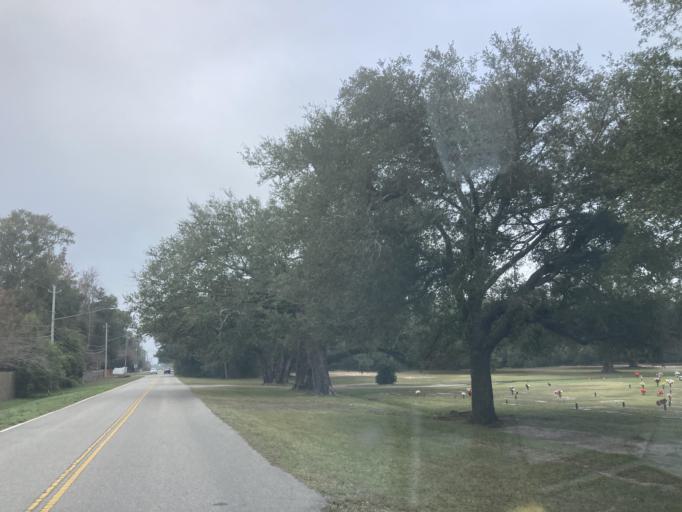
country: US
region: Mississippi
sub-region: Harrison County
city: West Gulfport
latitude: 30.4106
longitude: -89.0312
